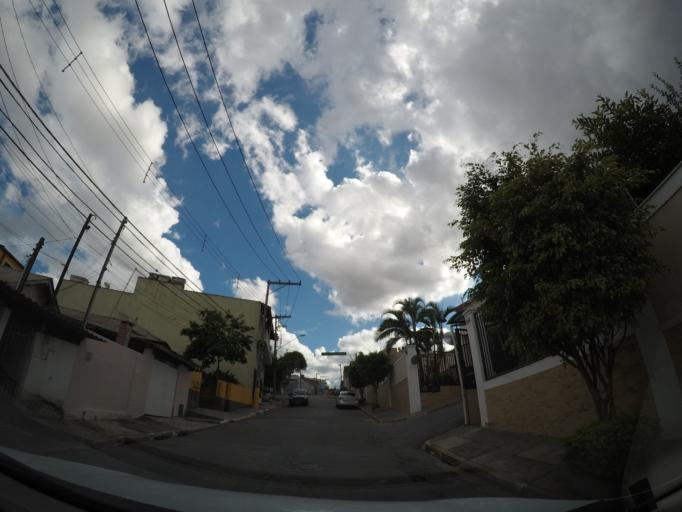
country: BR
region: Sao Paulo
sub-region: Guarulhos
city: Guarulhos
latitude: -23.4822
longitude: -46.5490
